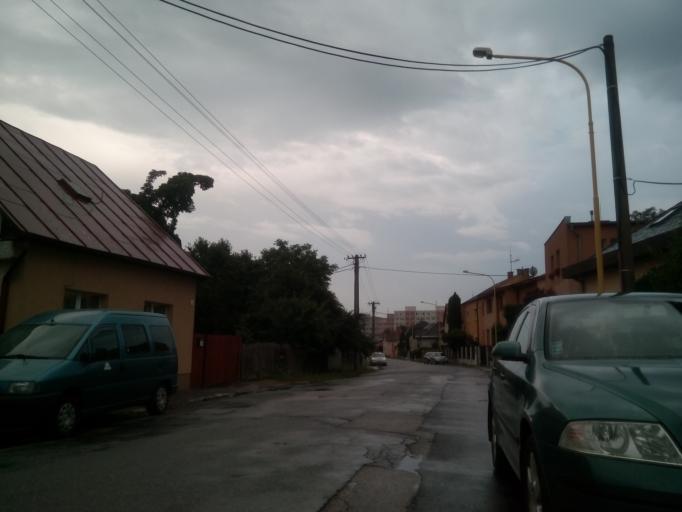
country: SK
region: Kosicky
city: Kosice
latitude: 48.7354
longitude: 21.2586
